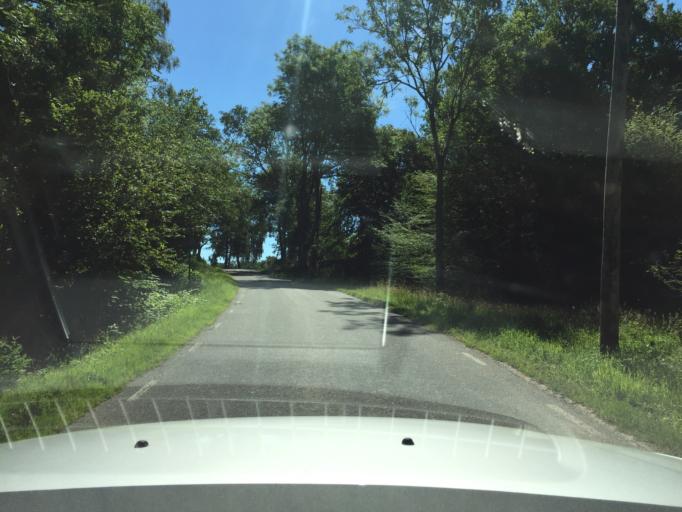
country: SE
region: Skane
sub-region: Hassleholms Kommun
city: Sosdala
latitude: 56.0192
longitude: 13.5849
